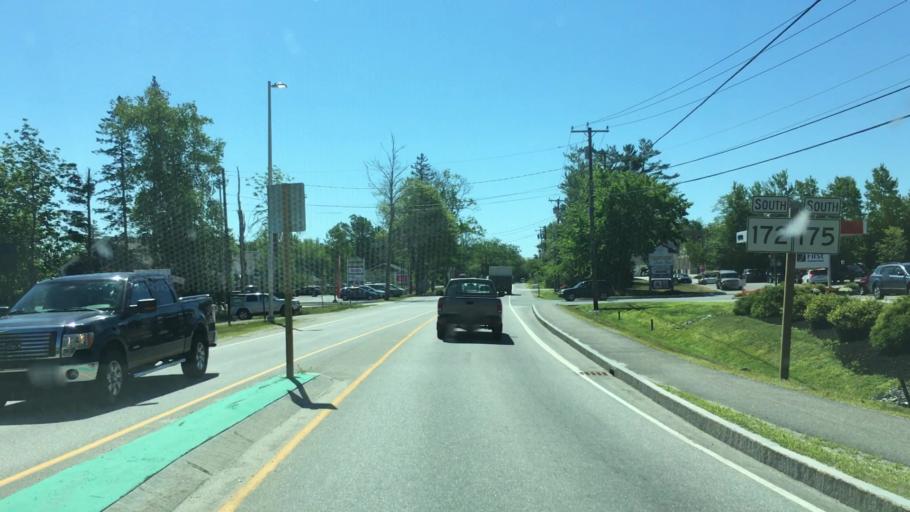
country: US
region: Maine
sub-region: Hancock County
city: Sedgwick
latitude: 44.4078
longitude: -68.5974
